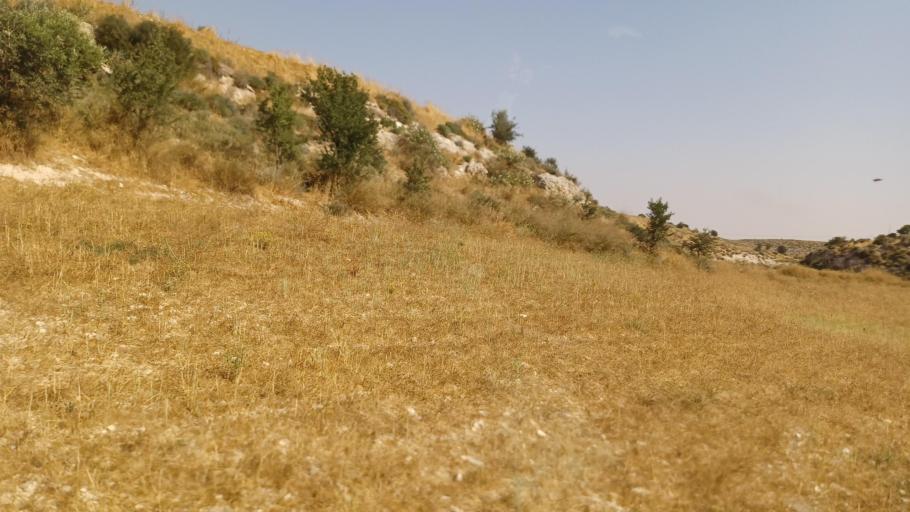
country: CY
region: Lefkosia
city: Lympia
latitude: 34.9786
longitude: 33.4799
